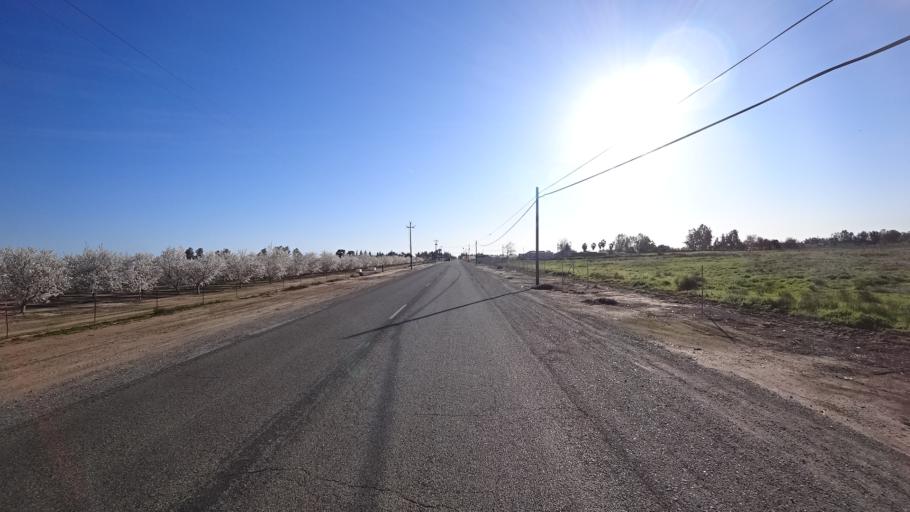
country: US
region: California
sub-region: Fresno County
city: West Park
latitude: 36.7788
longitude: -119.9193
